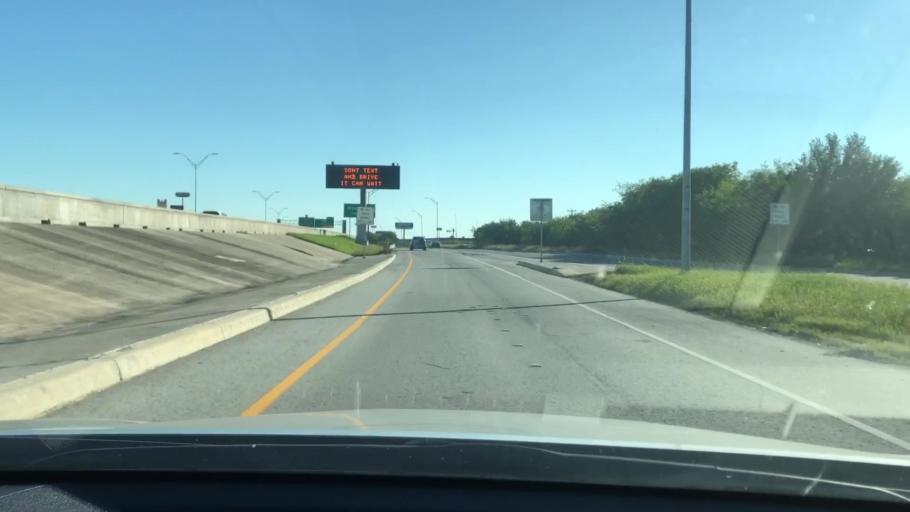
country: US
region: Texas
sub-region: Bexar County
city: Windcrest
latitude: 29.5182
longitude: -98.3962
